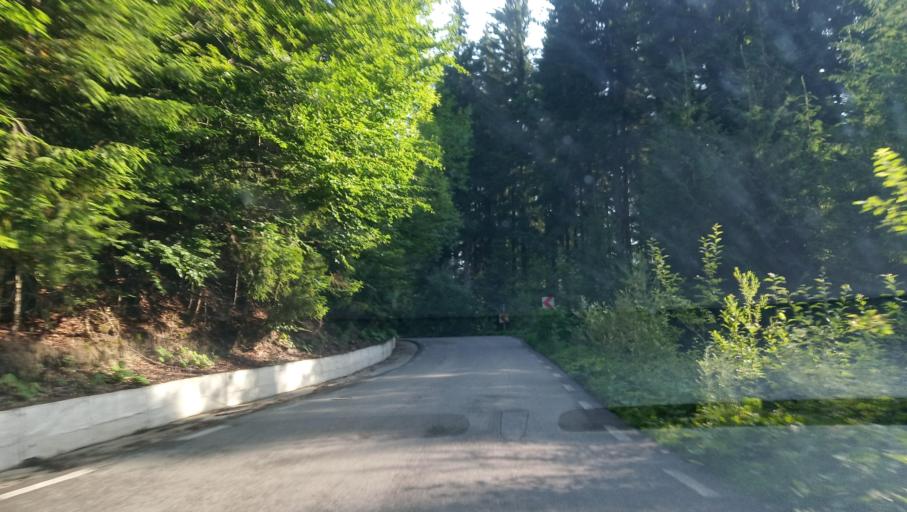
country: RO
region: Prahova
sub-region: Oras Sinaia
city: Sinaia
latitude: 45.3167
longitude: 25.5168
